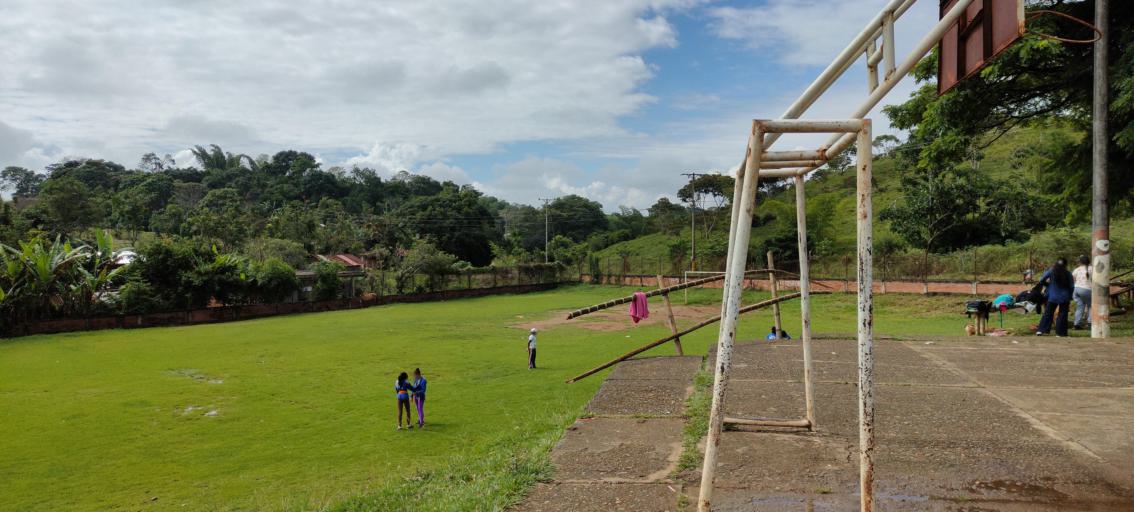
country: CO
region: Cauca
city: Buenos Aires
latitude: 3.1203
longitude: -76.6049
